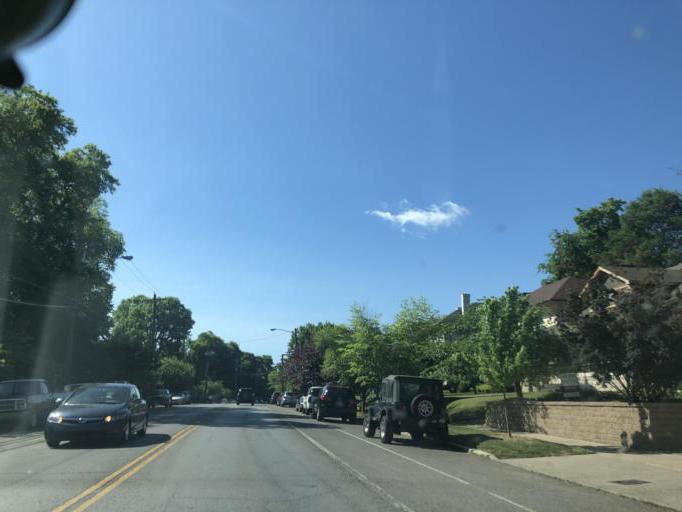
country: US
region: Tennessee
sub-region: Davidson County
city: Nashville
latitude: 36.1286
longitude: -86.7950
